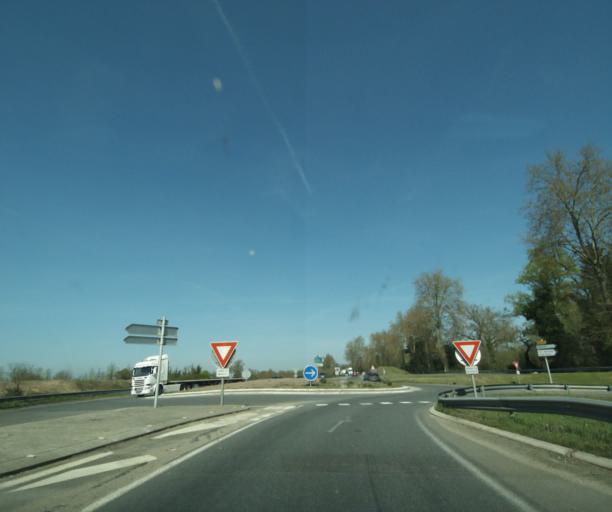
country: FR
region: Auvergne
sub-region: Departement de l'Allier
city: Trevol
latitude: 46.6246
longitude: 3.2864
